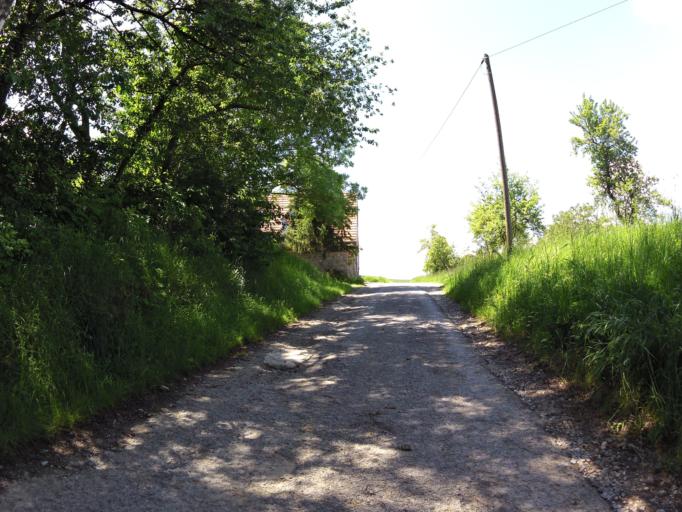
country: DE
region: Bavaria
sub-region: Regierungsbezirk Unterfranken
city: Theilheim
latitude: 49.7323
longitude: 10.0368
